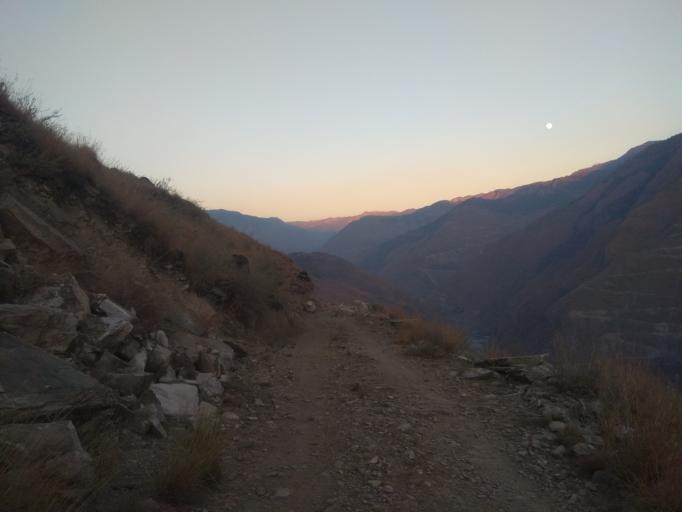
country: NP
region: Mid Western
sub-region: Bheri Zone
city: Dailekh
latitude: 29.2650
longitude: 81.6901
